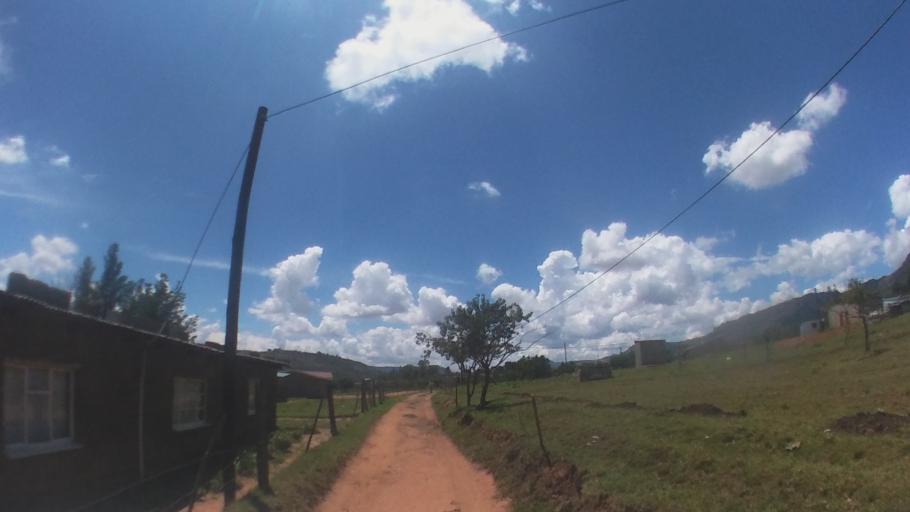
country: LS
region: Maseru
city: Nako
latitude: -29.6210
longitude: 27.5178
